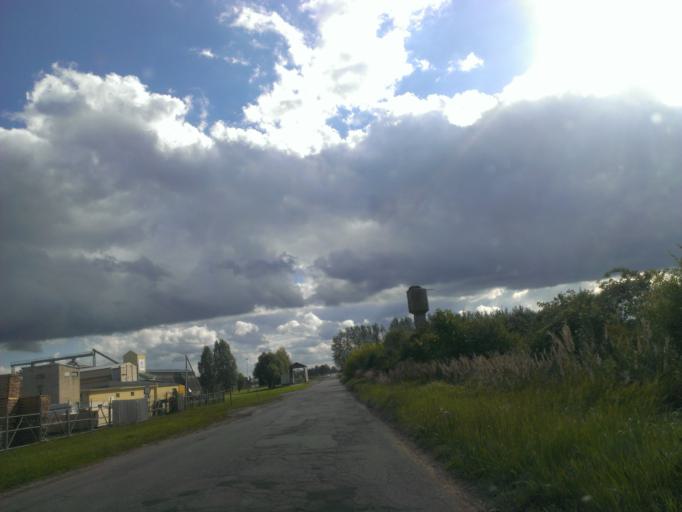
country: LV
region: Sigulda
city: Sigulda
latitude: 57.1439
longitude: 24.8927
